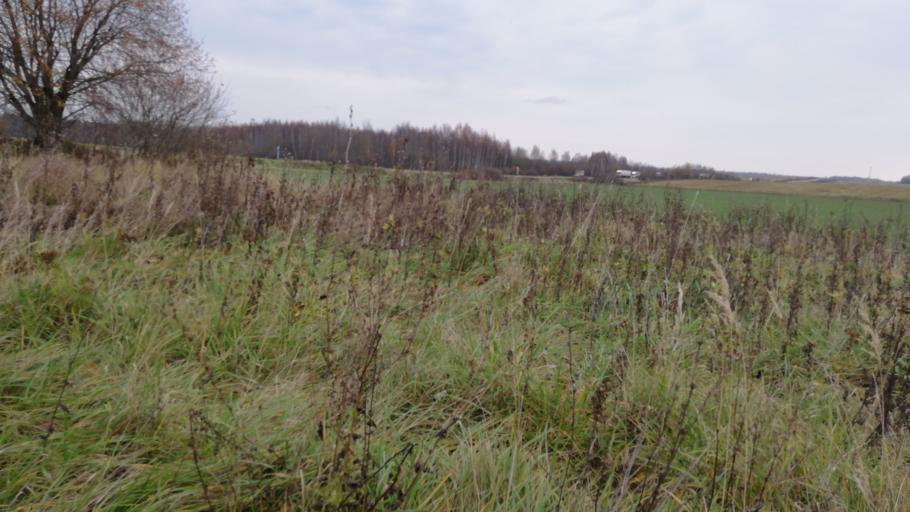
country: RU
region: Ivanovo
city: Pistsovo
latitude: 57.1841
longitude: 40.4617
